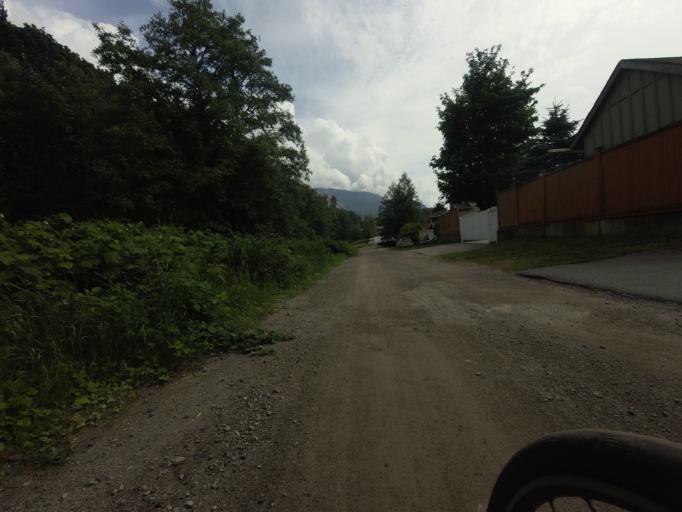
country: CA
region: British Columbia
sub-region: Greater Vancouver Regional District
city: Lions Bay
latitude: 49.7115
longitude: -123.1527
